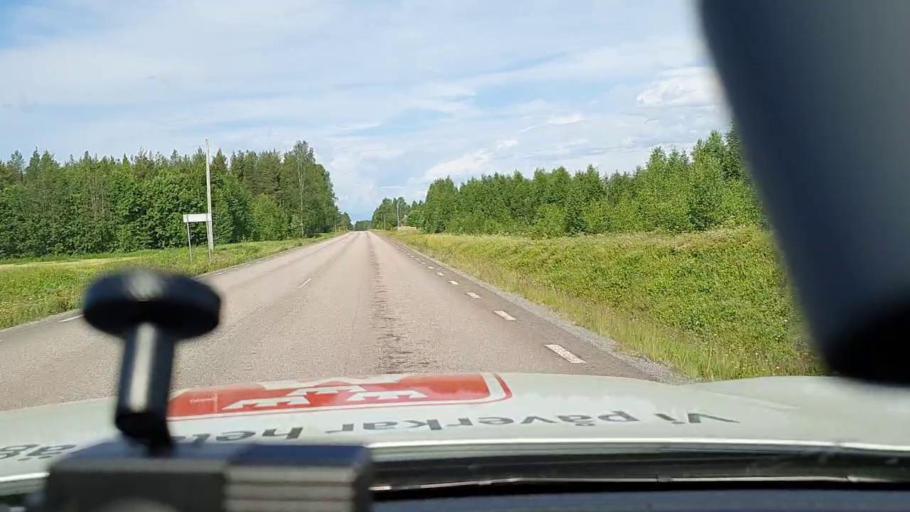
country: SE
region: Norrbotten
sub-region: Alvsbyns Kommun
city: AElvsbyn
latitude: 66.0166
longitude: 21.1549
